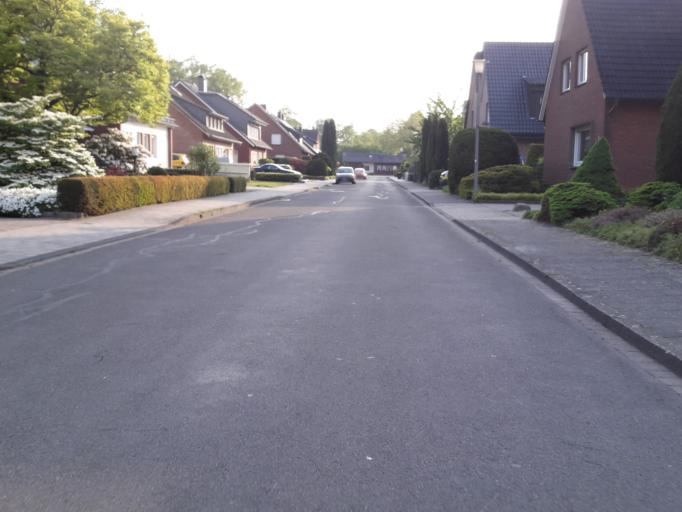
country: DE
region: North Rhine-Westphalia
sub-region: Regierungsbezirk Munster
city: Muenster
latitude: 51.9094
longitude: 7.6580
